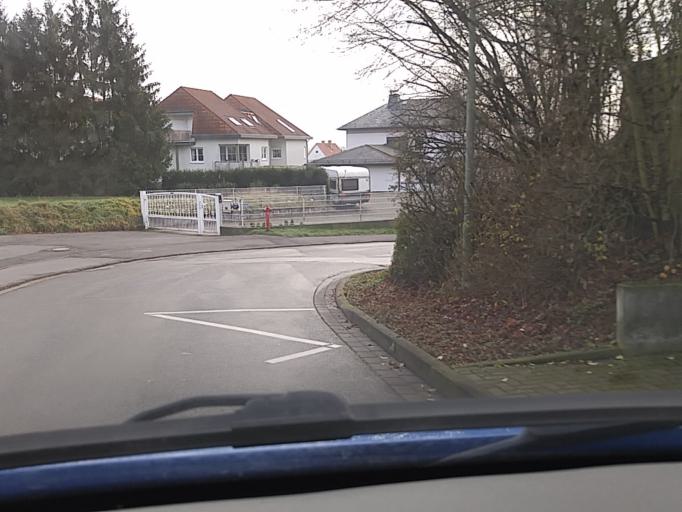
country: DE
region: Hesse
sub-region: Regierungsbezirk Darmstadt
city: Friedberg
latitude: 50.3543
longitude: 8.7710
